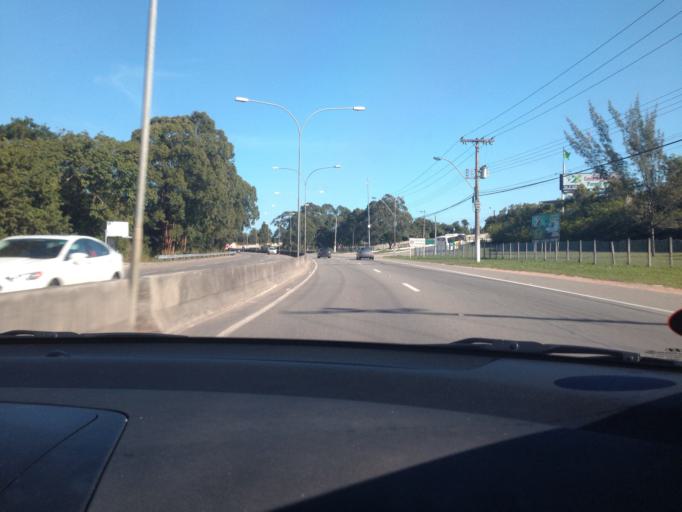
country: BR
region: Espirito Santo
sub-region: Viana
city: Viana
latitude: -20.5013
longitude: -40.3638
